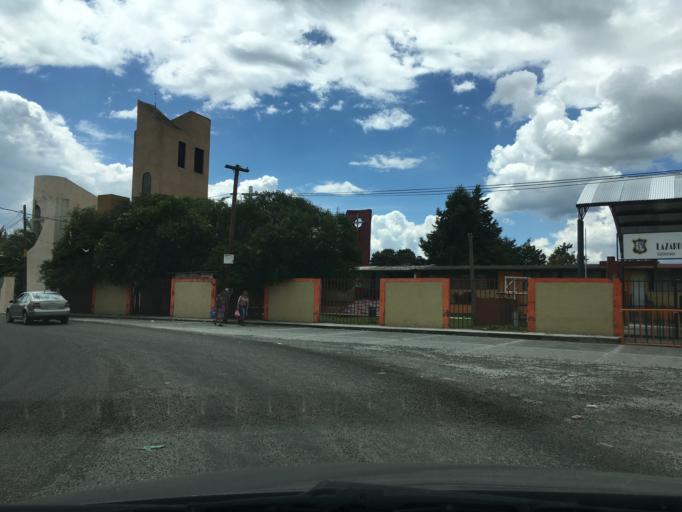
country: MX
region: Michoacan
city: Zacapu
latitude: 19.8362
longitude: -101.7277
